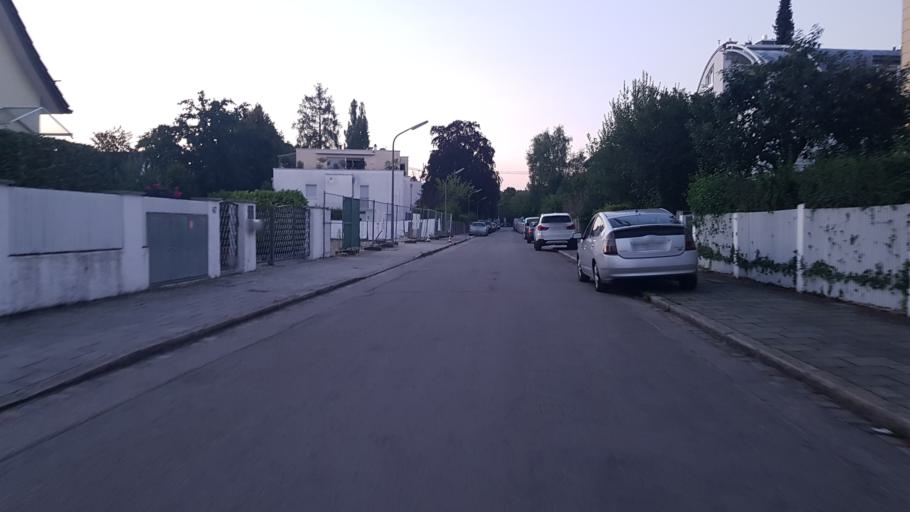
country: DE
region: Bavaria
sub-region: Upper Bavaria
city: Pasing
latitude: 48.1381
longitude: 11.4919
